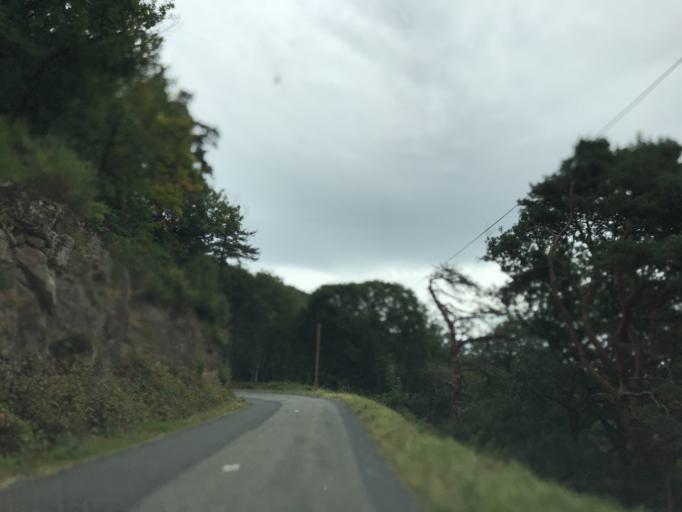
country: FR
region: Rhone-Alpes
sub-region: Departement de la Loire
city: Sail-sous-Couzan
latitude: 45.6859
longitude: 3.9046
